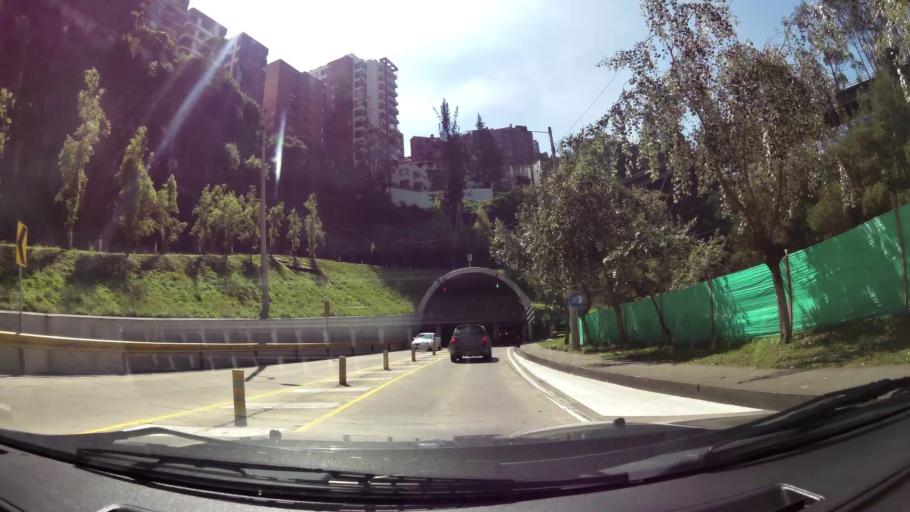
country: EC
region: Pichincha
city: Quito
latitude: -0.1899
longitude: -78.4784
